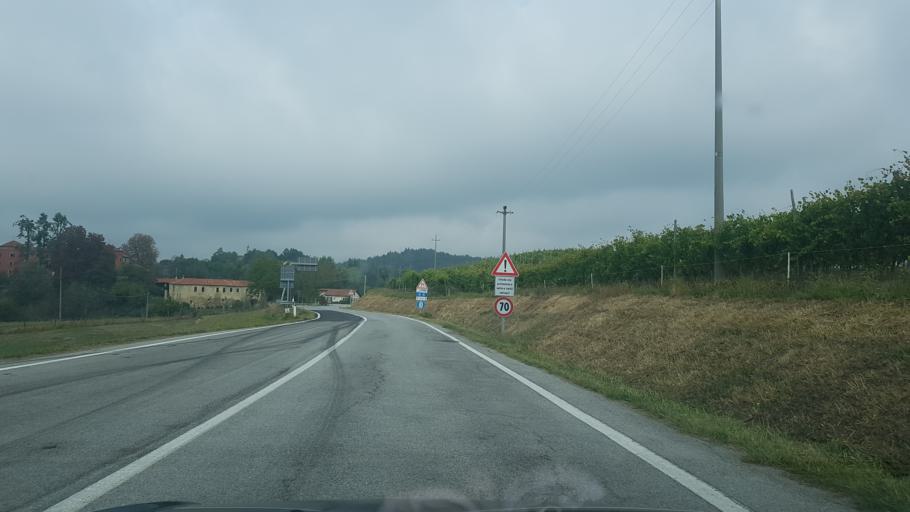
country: IT
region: Piedmont
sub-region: Provincia di Cuneo
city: Camerana
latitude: 44.4020
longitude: 8.1171
